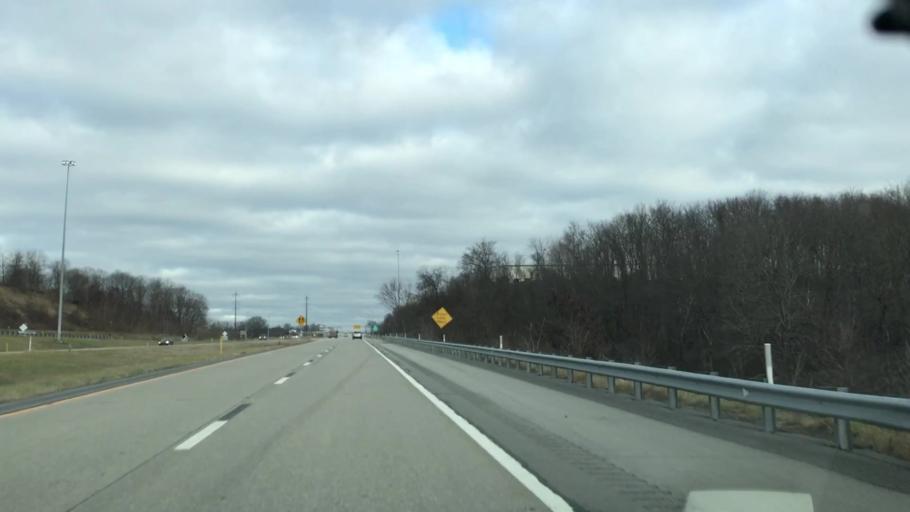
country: US
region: Pennsylvania
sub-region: Allegheny County
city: Carnot-Moon
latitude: 40.5240
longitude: -80.2722
